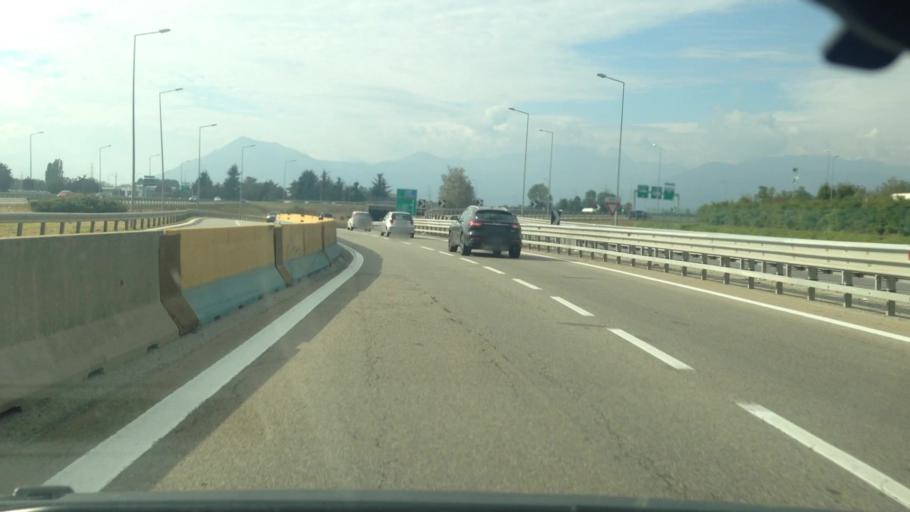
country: IT
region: Piedmont
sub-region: Provincia di Torino
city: Savonera
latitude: 45.1046
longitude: 7.6058
